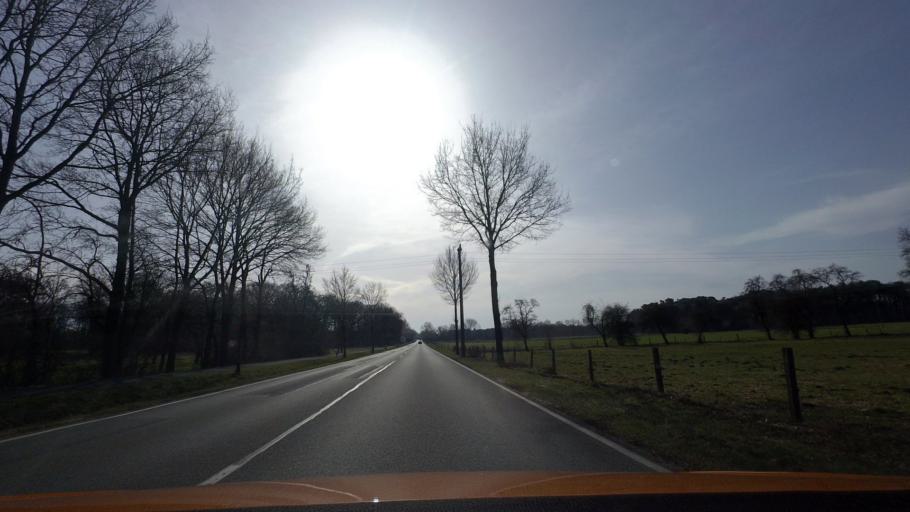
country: DE
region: Lower Saxony
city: Raddestorf
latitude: 52.4494
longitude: 8.9269
